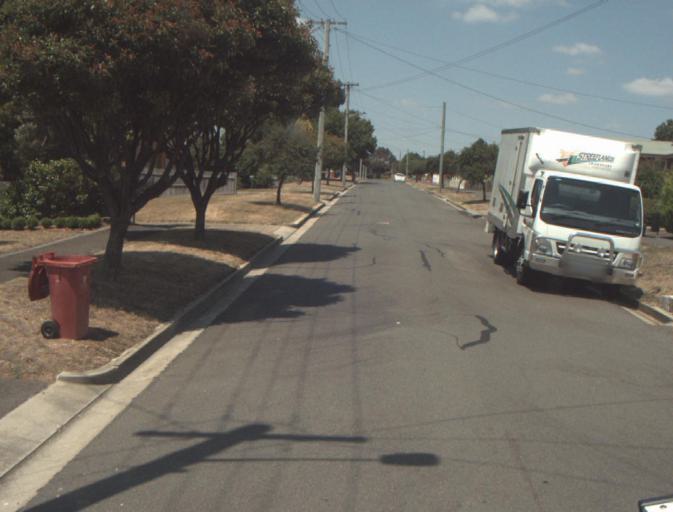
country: AU
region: Tasmania
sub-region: Launceston
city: Summerhill
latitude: -41.4858
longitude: 147.1733
